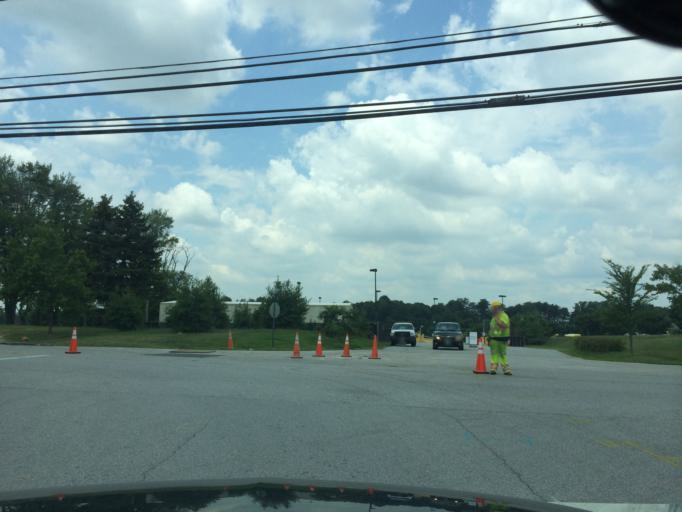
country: US
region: Maryland
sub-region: Howard County
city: Hanover
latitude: 39.1801
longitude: -76.7076
